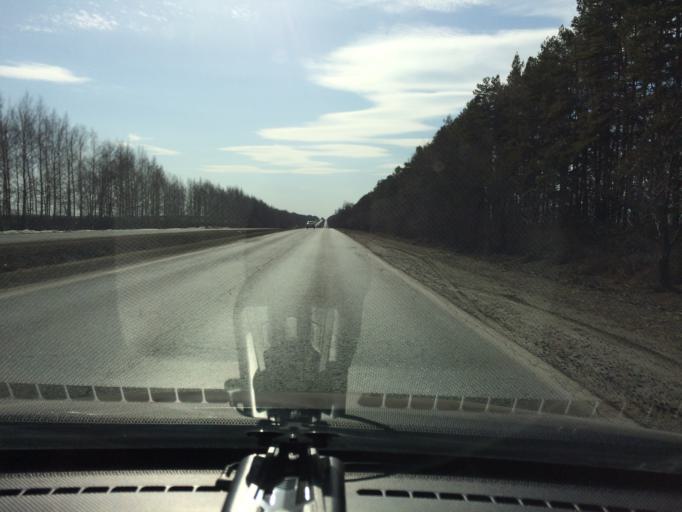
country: RU
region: Mariy-El
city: Surok
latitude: 56.7369
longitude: 48.1699
